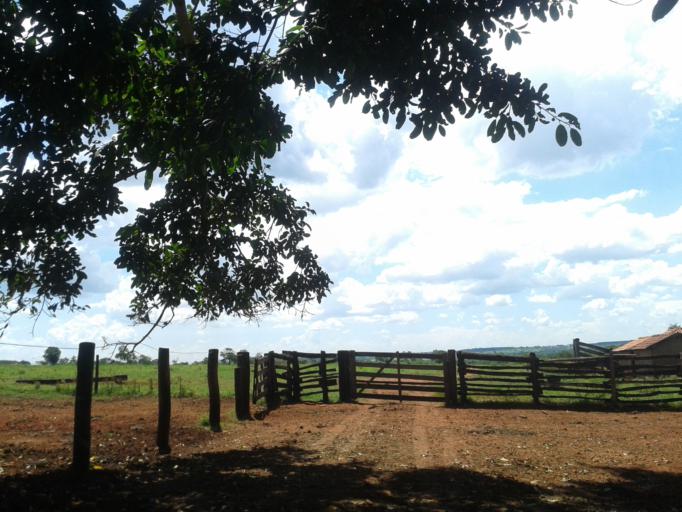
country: BR
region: Minas Gerais
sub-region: Santa Vitoria
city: Santa Vitoria
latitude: -19.1142
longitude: -50.5169
